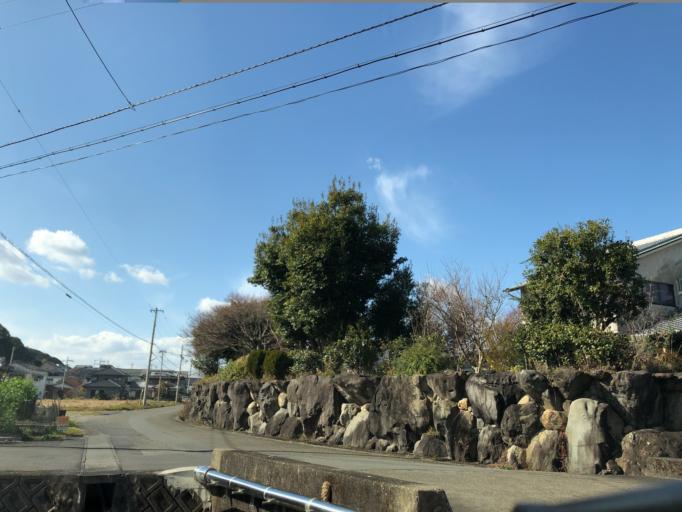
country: JP
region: Kochi
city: Sukumo
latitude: 32.9274
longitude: 132.6863
